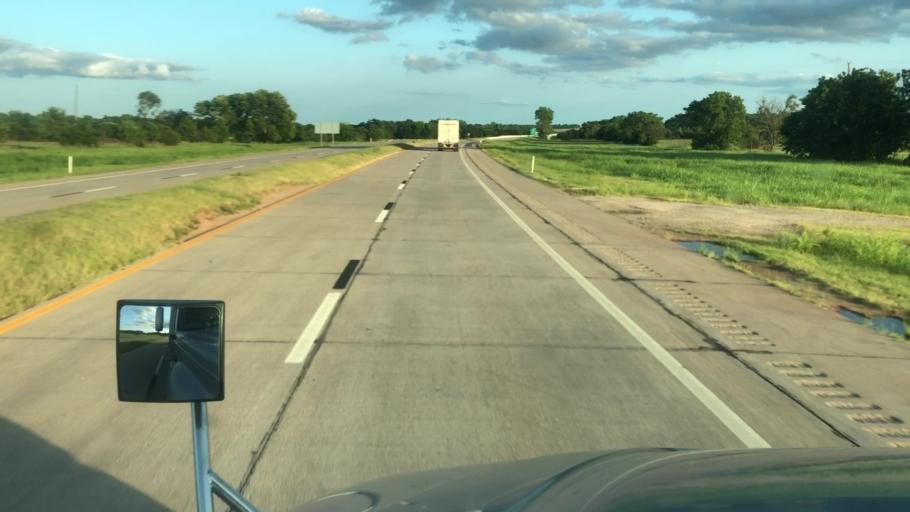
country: US
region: Oklahoma
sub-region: Pawnee County
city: Pawnee
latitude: 36.3159
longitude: -96.9945
